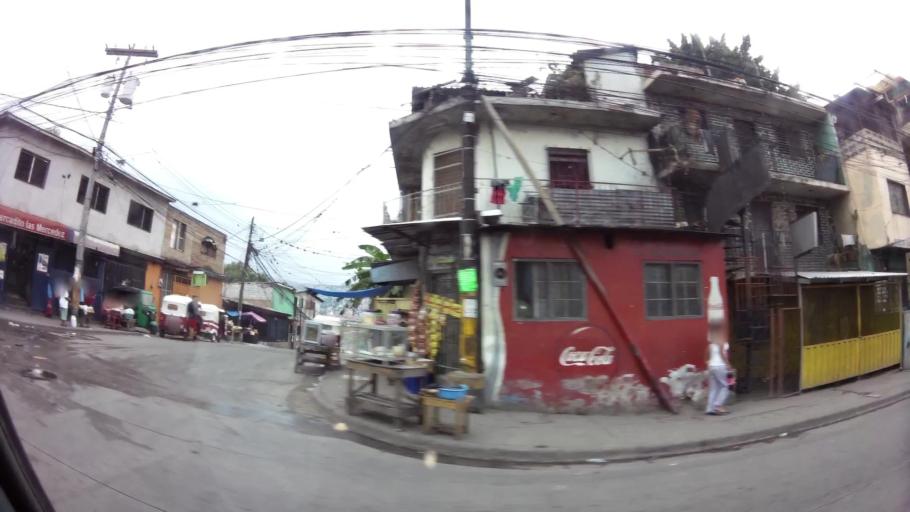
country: HN
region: Francisco Morazan
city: Tegucigalpa
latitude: 14.0971
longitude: -87.2202
